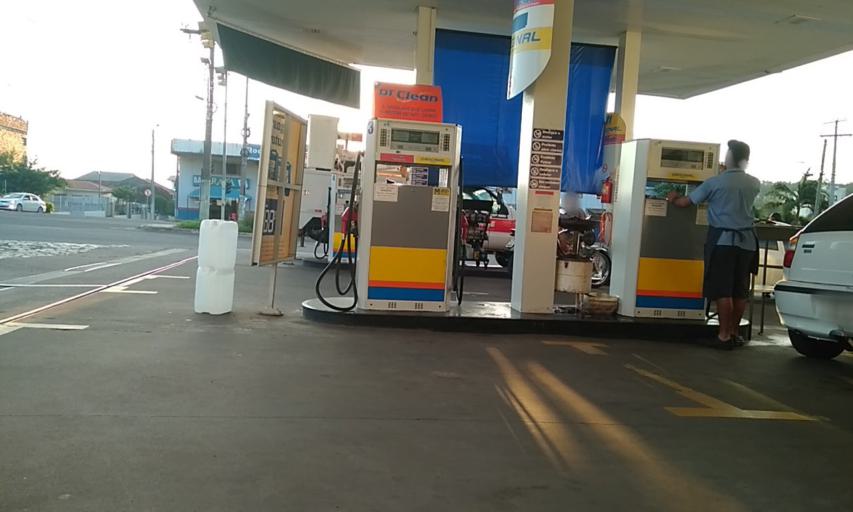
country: BR
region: Rio Grande do Sul
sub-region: Taquara
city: Taquara
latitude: -29.6487
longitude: -50.7755
